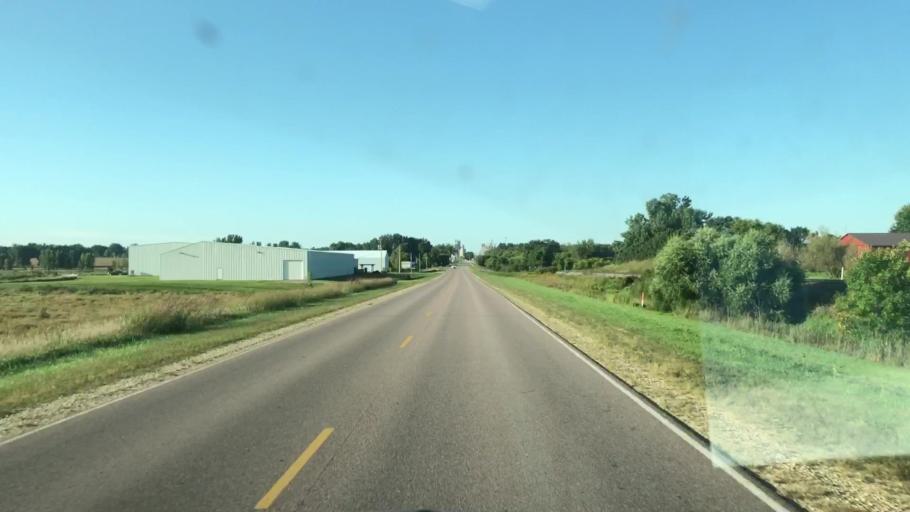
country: US
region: Iowa
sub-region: O'Brien County
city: Sheldon
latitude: 43.2013
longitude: -95.8462
